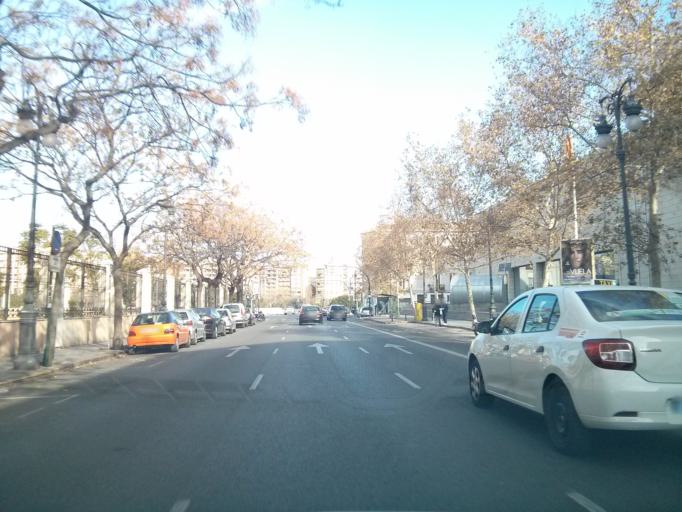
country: ES
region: Valencia
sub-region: Provincia de Valencia
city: Valencia
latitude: 39.4794
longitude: -0.3833
